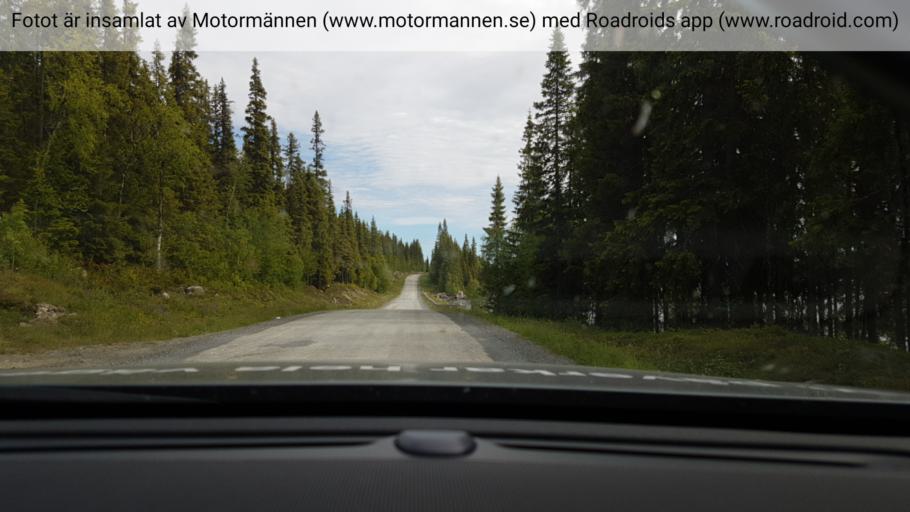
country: SE
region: Vaesterbotten
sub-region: Vilhelmina Kommun
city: Sjoberg
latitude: 65.1436
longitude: 16.2616
